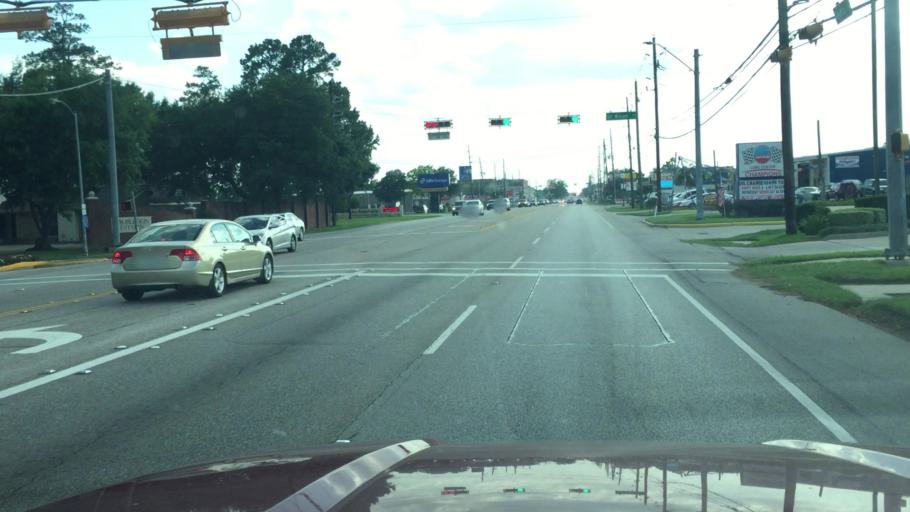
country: US
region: Texas
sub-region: Harris County
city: Spring
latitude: 30.0246
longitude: -95.5175
